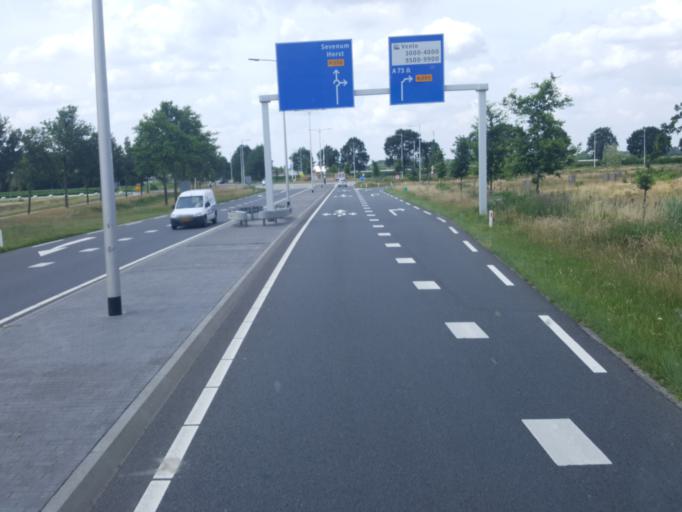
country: NL
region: Limburg
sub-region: Gemeente Peel en Maas
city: Maasbree
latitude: 51.4015
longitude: 6.0700
